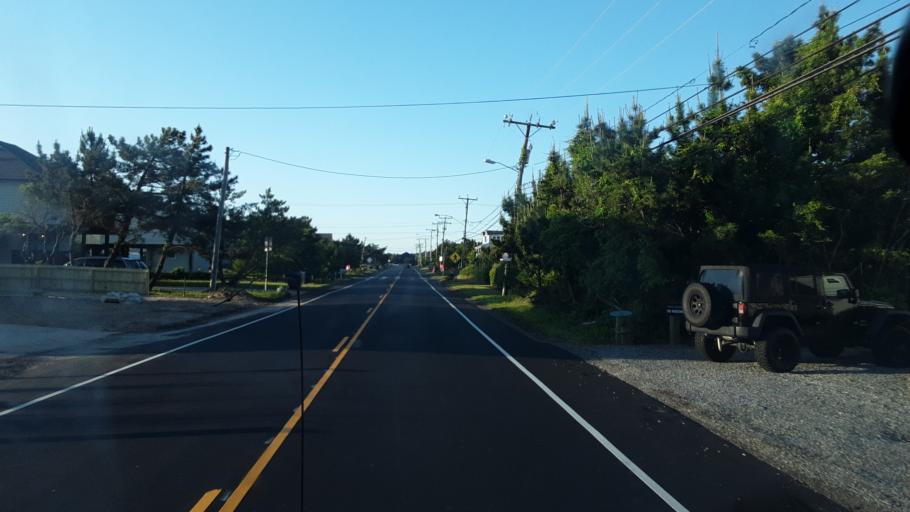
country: US
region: Virginia
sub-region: City of Virginia Beach
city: Virginia Beach
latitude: 36.7211
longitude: -75.9358
